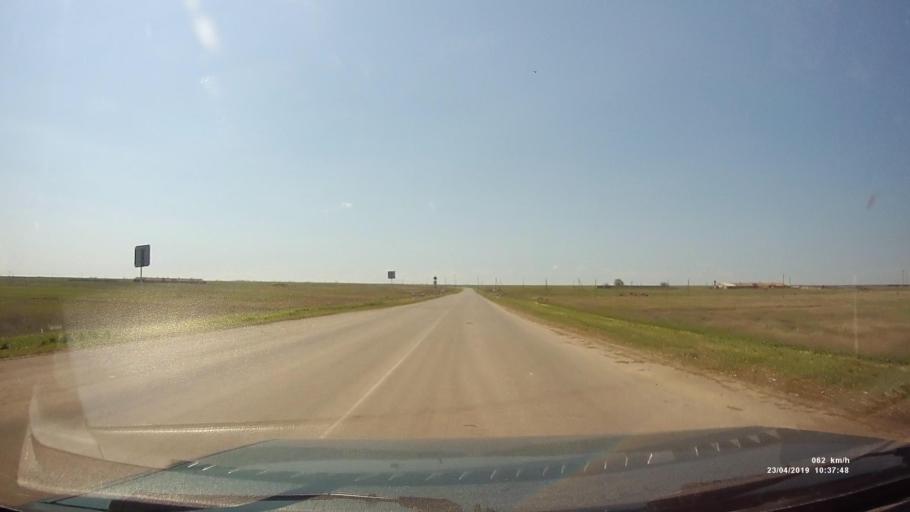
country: RU
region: Kalmykiya
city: Yashalta
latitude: 46.5400
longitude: 42.6402
